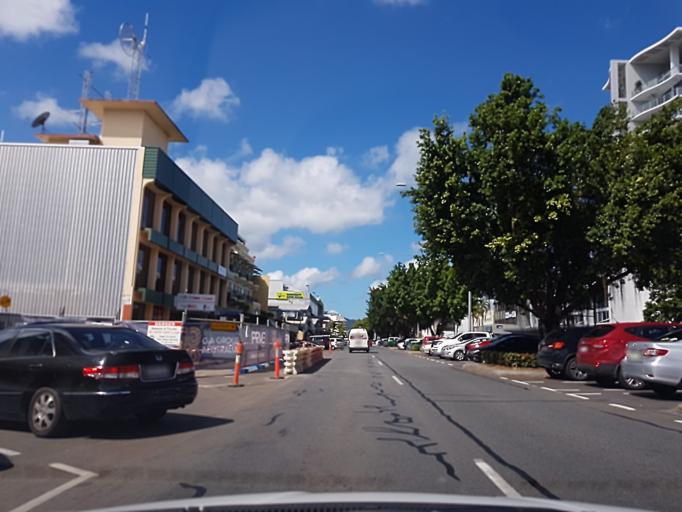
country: AU
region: Queensland
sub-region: Cairns
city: Cairns
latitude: -16.9198
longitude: 145.7756
